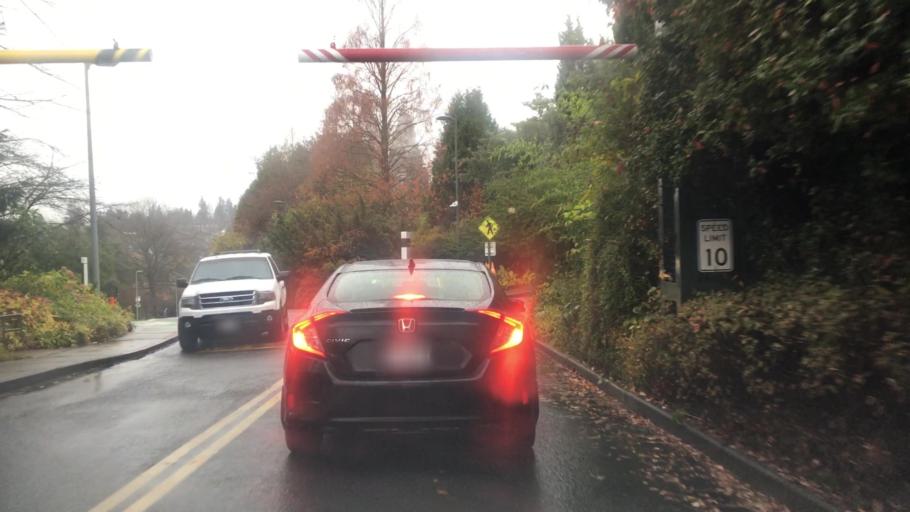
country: US
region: Washington
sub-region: King County
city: Yarrow Point
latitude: 47.6630
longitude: -122.2806
